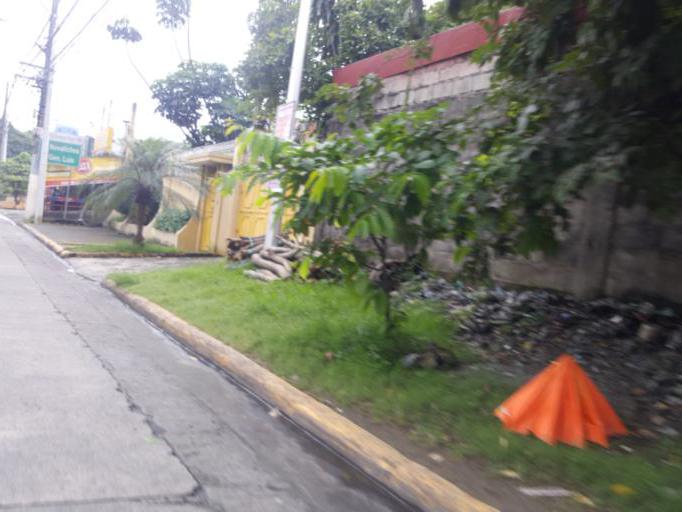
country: PH
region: Calabarzon
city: Bagong Pagasa
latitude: 14.6995
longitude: 121.0233
